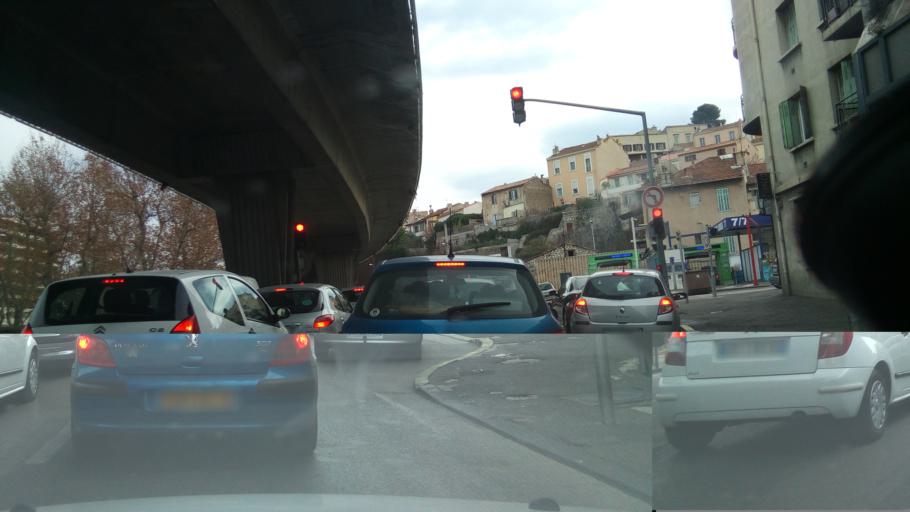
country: FR
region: Provence-Alpes-Cote d'Azur
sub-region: Departement des Bouches-du-Rhone
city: Marseille 01
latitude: 43.3143
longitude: 5.3881
